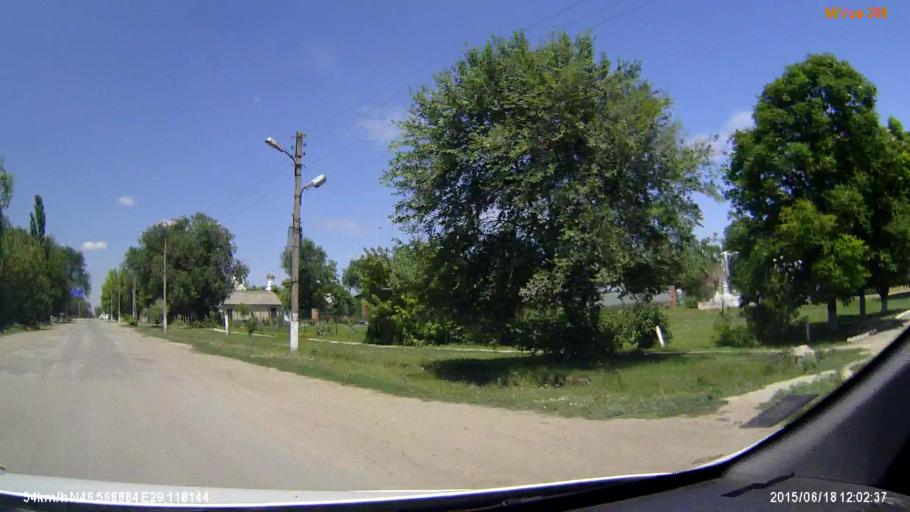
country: MD
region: Basarabeasca
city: Basarabeasca
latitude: 46.5667
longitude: 29.1184
